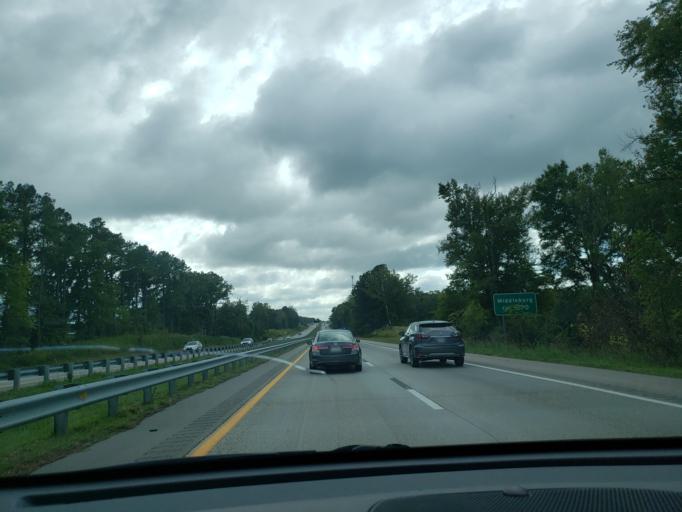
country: US
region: North Carolina
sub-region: Vance County
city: Henderson
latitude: 36.4050
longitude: -78.3282
